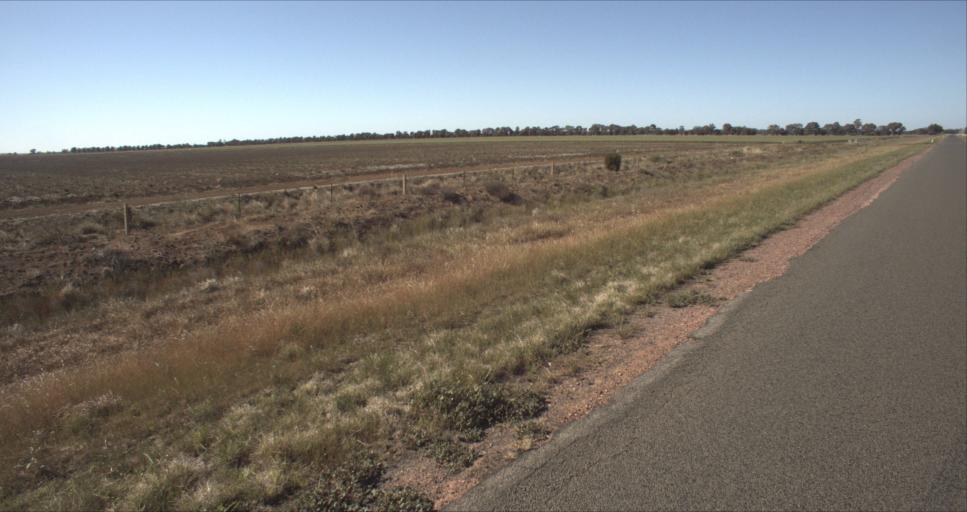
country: AU
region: New South Wales
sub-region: Leeton
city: Leeton
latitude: -34.5708
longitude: 146.2635
